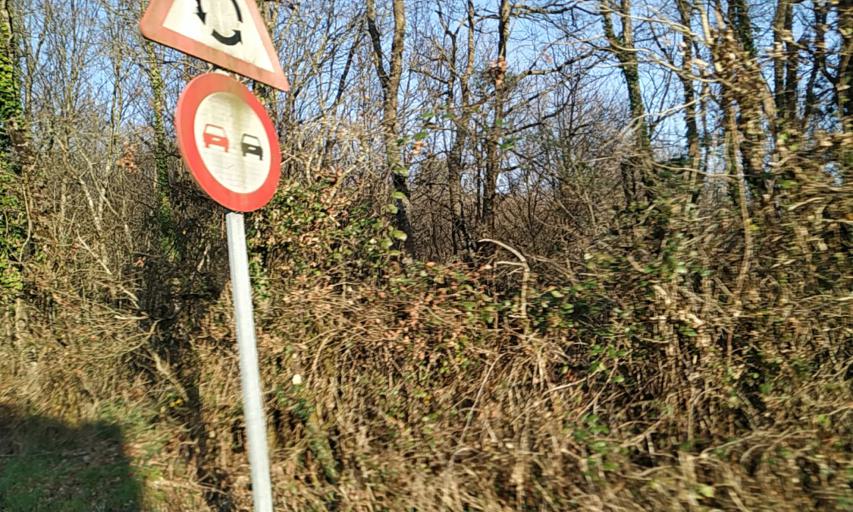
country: ES
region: Galicia
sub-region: Provincia de Lugo
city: Corgo
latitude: 42.9377
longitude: -7.3982
